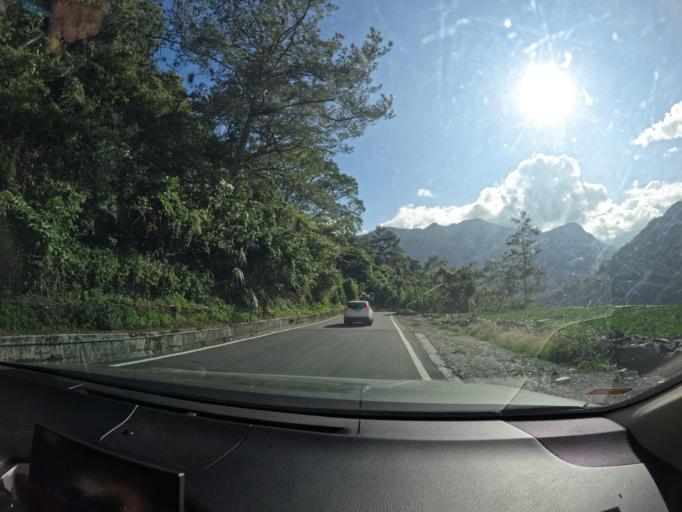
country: TW
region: Taiwan
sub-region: Taitung
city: Taitung
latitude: 23.1986
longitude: 121.0193
